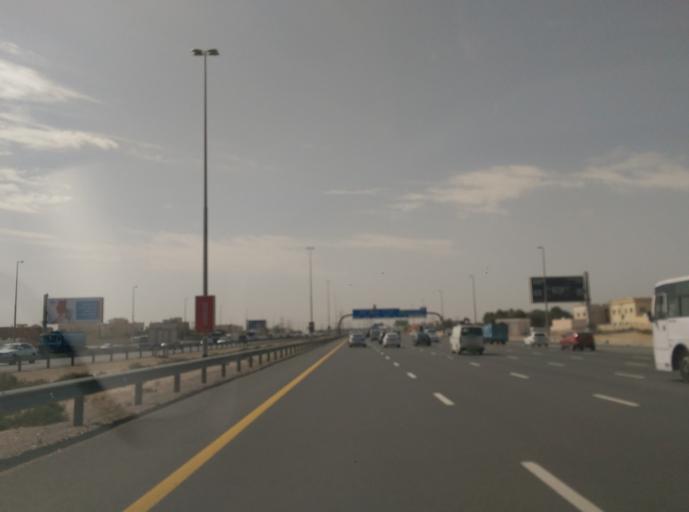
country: AE
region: Dubai
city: Dubai
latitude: 25.1583
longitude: 55.2615
